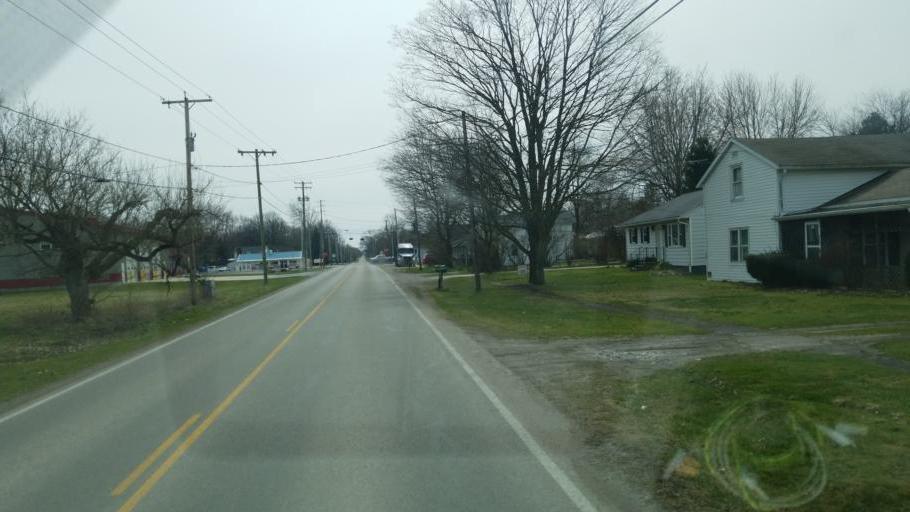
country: US
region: Ohio
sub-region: Huron County
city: Wakeman
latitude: 41.2497
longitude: -82.4916
